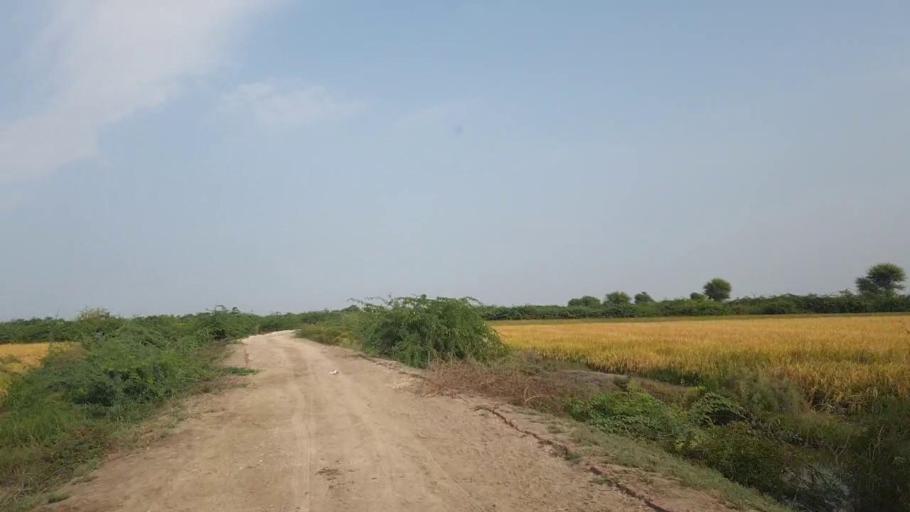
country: PK
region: Sindh
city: Kadhan
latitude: 24.4436
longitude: 68.8018
